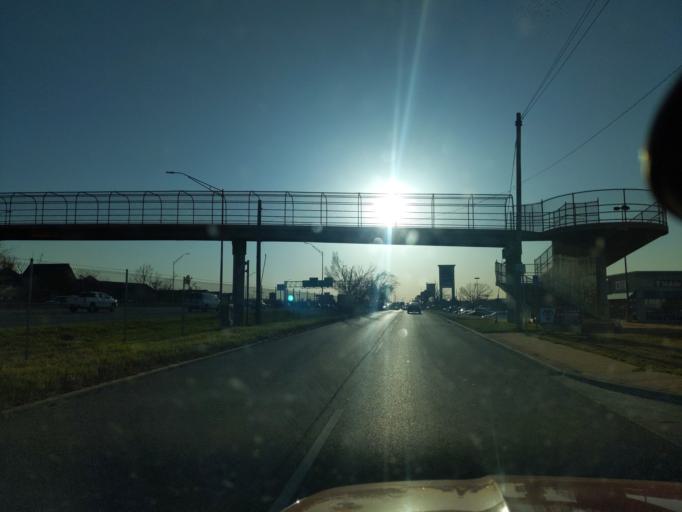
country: US
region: Oklahoma
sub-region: Cleveland County
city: Moore
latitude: 35.3917
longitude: -97.5391
